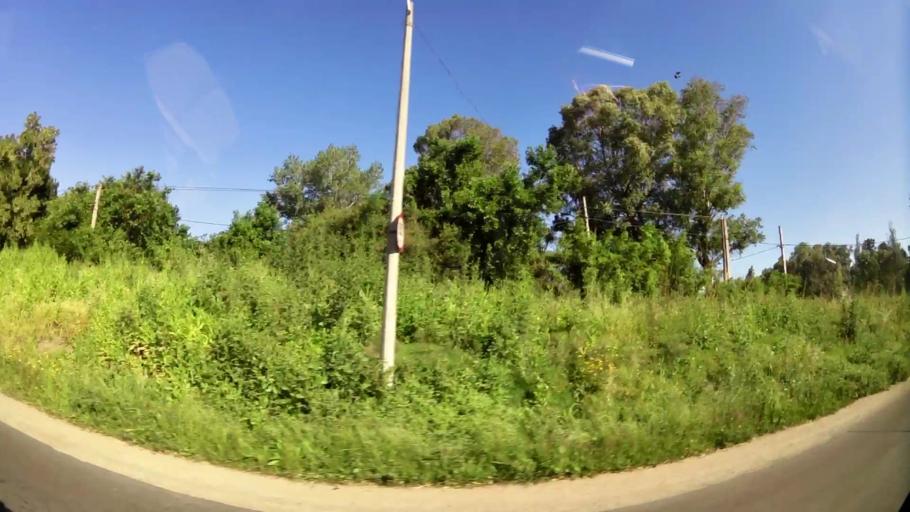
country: UY
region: Canelones
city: La Paz
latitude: -34.8085
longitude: -56.1641
